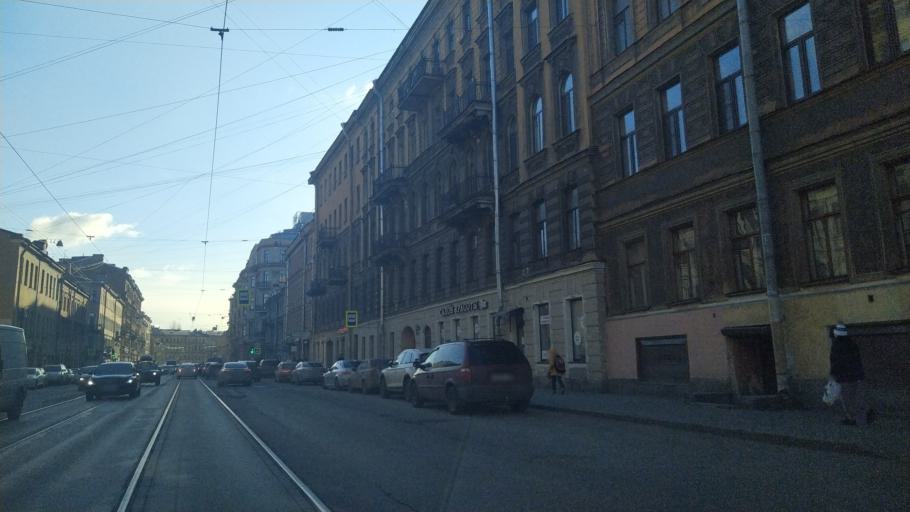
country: RU
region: St.-Petersburg
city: Centralniy
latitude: 59.9256
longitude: 30.3516
